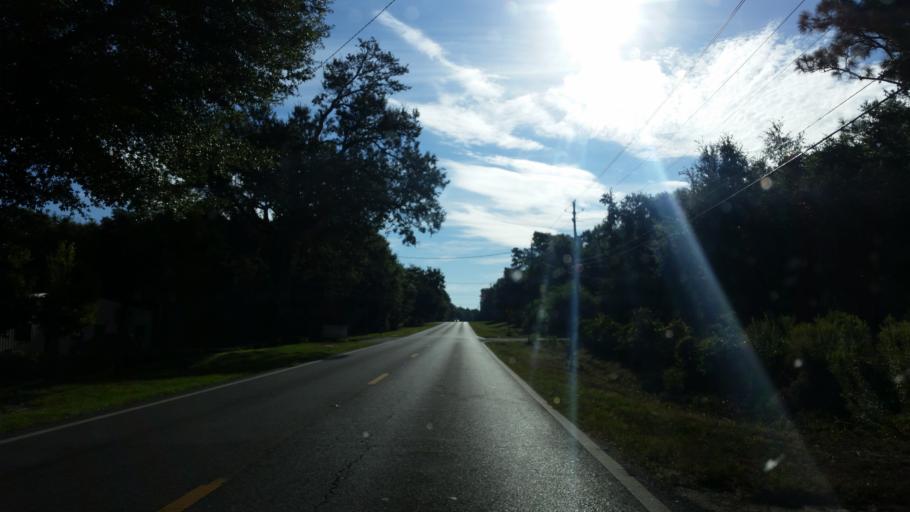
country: US
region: Florida
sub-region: Santa Rosa County
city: Bagdad
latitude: 30.6021
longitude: -87.0676
